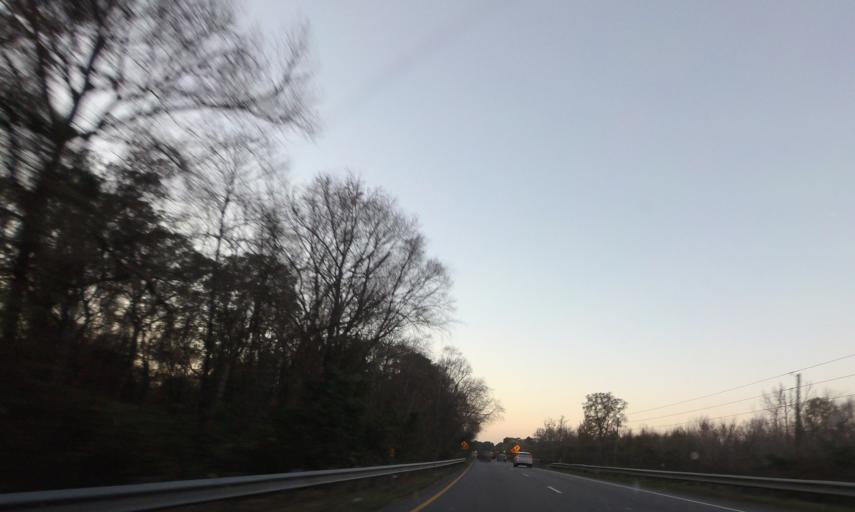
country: US
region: Georgia
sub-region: Houston County
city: Warner Robins
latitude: 32.6684
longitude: -83.6209
